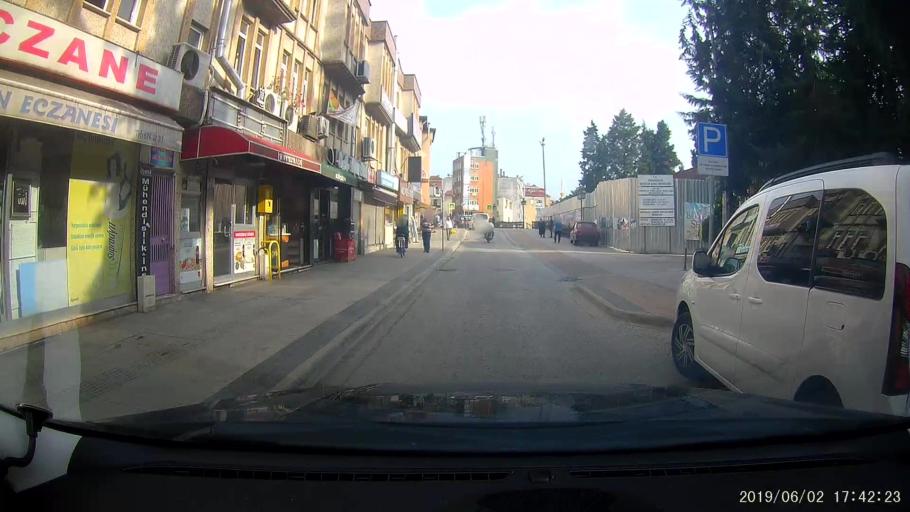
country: TR
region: Samsun
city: Terme
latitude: 41.2089
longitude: 36.9721
